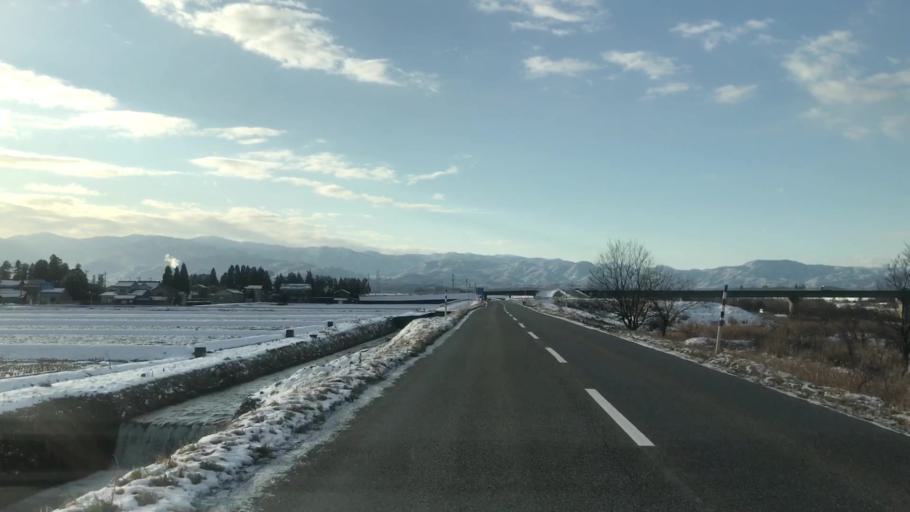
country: JP
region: Toyama
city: Toyama-shi
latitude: 36.6525
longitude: 137.2858
